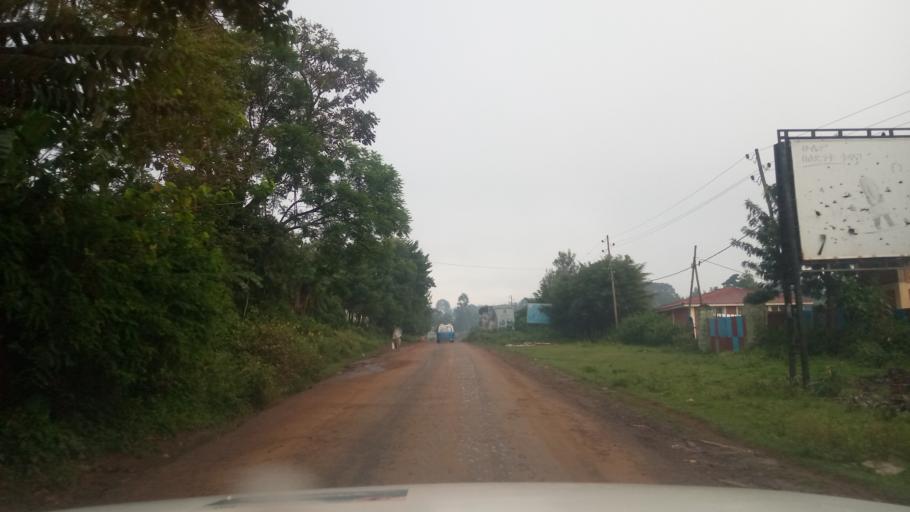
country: ET
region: Oromiya
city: Jima
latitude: 7.6932
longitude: 36.8214
